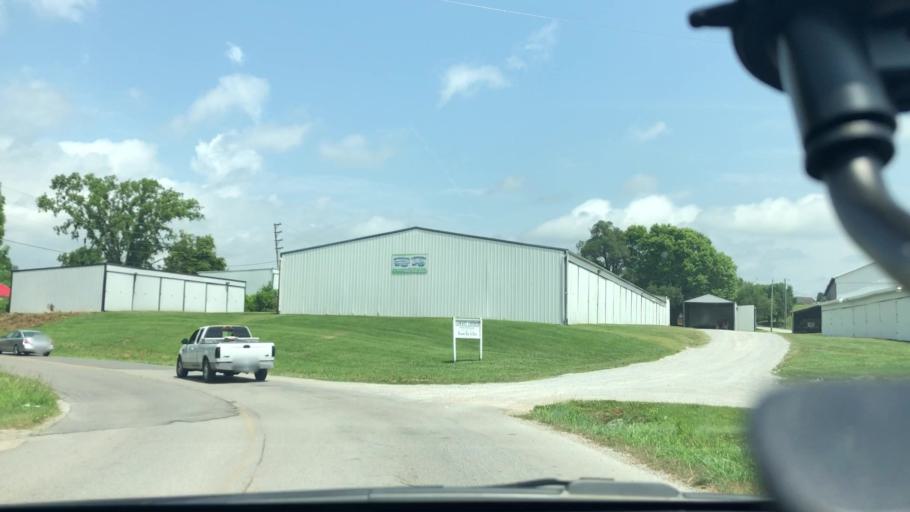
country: US
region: Kentucky
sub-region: Pulaski County
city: Somerset
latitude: 37.0620
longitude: -84.6734
